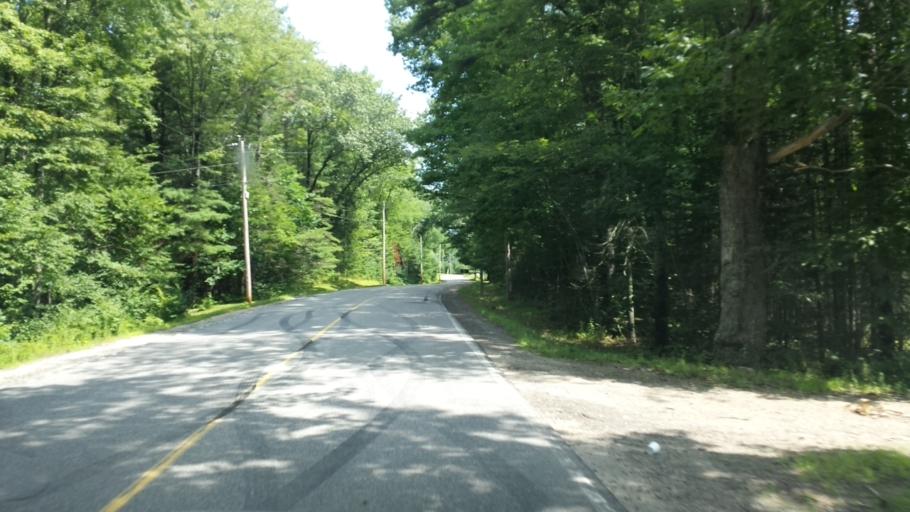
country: US
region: Maine
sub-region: York County
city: Kennebunk
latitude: 43.4427
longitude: -70.5274
